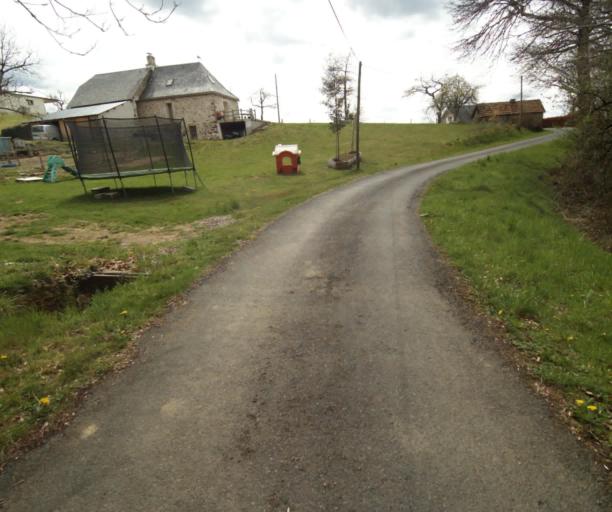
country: FR
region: Limousin
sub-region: Departement de la Correze
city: Laguenne
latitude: 45.2214
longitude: 1.8680
